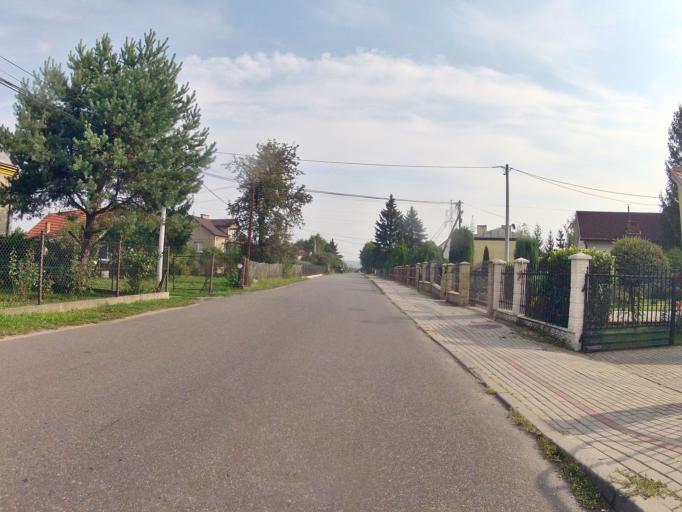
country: PL
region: Subcarpathian Voivodeship
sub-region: Powiat jasielski
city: Jaslo
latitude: 49.7308
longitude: 21.4491
